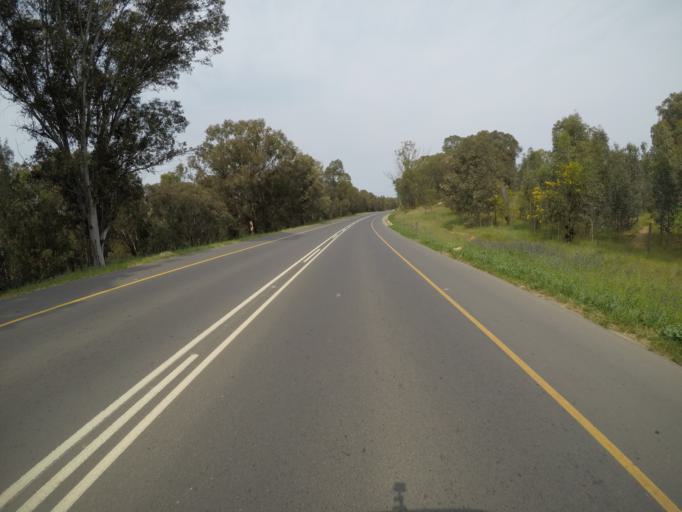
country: ZA
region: Western Cape
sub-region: West Coast District Municipality
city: Malmesbury
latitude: -33.4578
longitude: 18.7471
